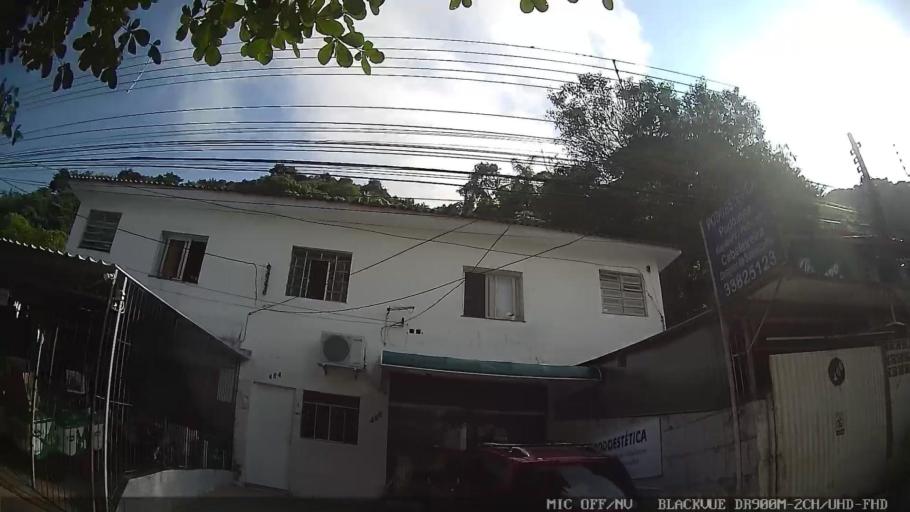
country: BR
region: Sao Paulo
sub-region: Guaruja
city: Guaruja
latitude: -23.9939
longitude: -46.2603
